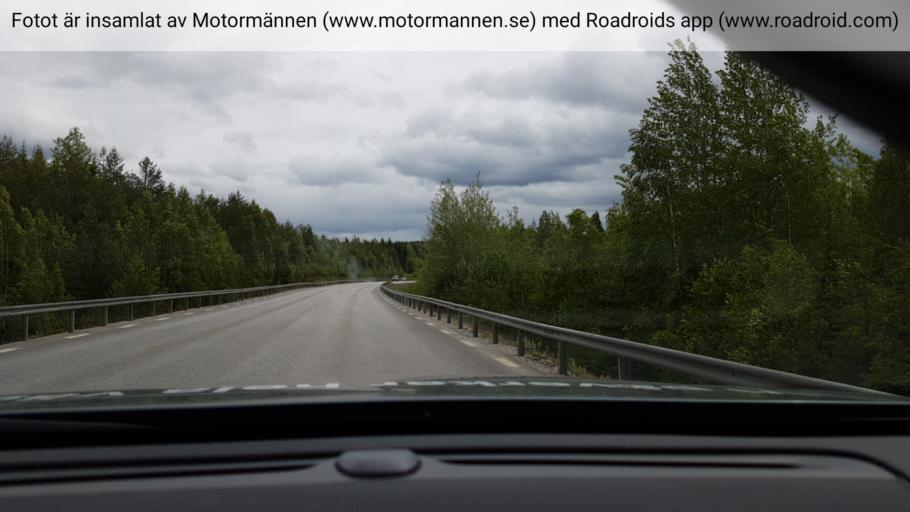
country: SE
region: Vaesterbotten
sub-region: Vannas Kommun
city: Vaennaes
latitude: 63.9463
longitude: 19.7631
